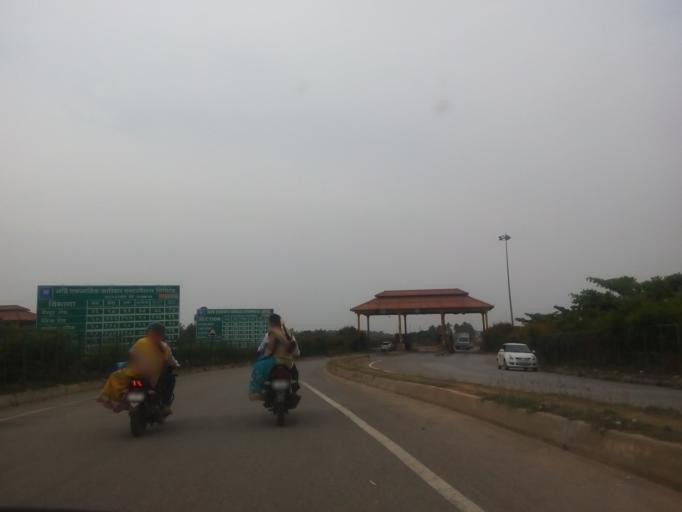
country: IN
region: Karnataka
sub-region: Bangalore Urban
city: Bangalore
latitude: 12.9891
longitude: 77.4727
